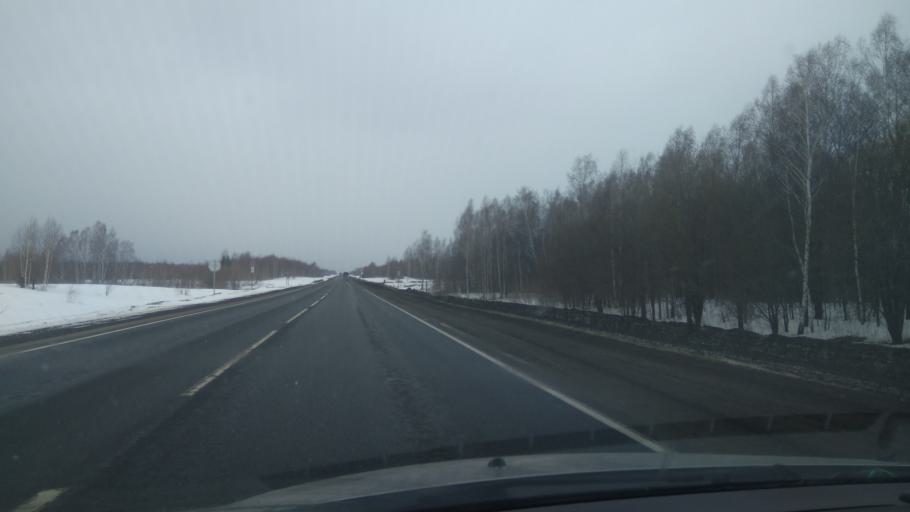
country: RU
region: Perm
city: Orda
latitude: 57.2085
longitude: 57.0976
